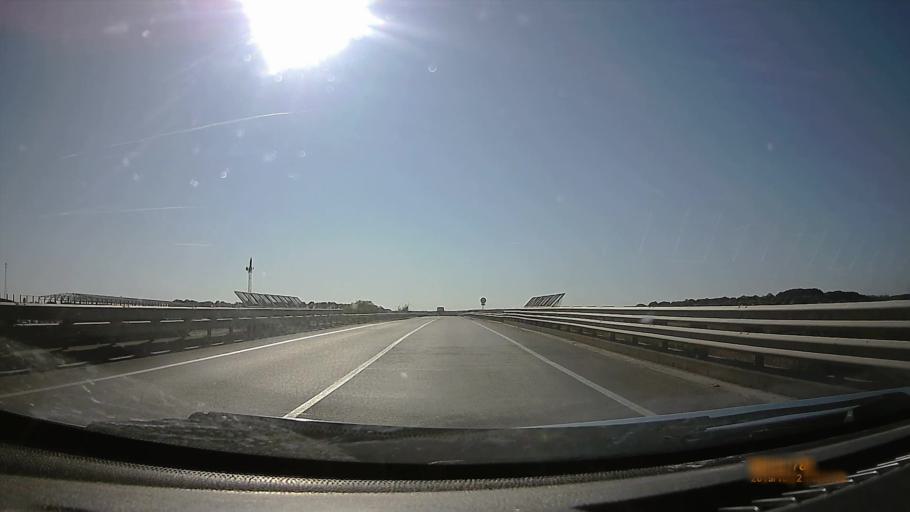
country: HU
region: Hajdu-Bihar
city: Biharkeresztes
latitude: 47.1392
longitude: 21.7075
